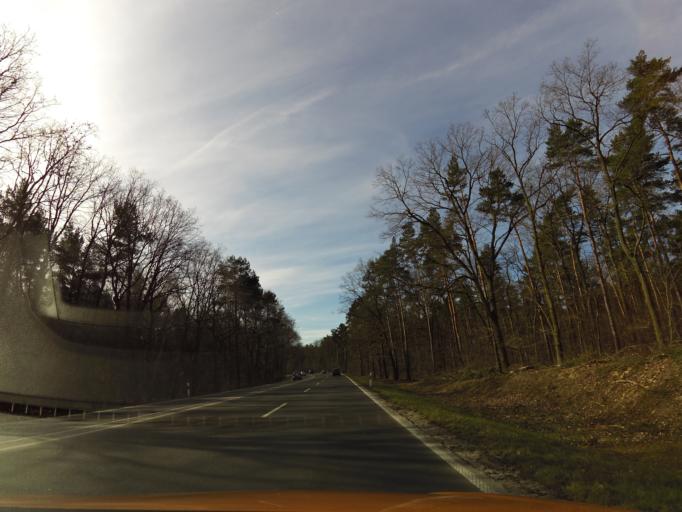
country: DE
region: Brandenburg
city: Potsdam
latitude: 52.3671
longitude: 13.0462
